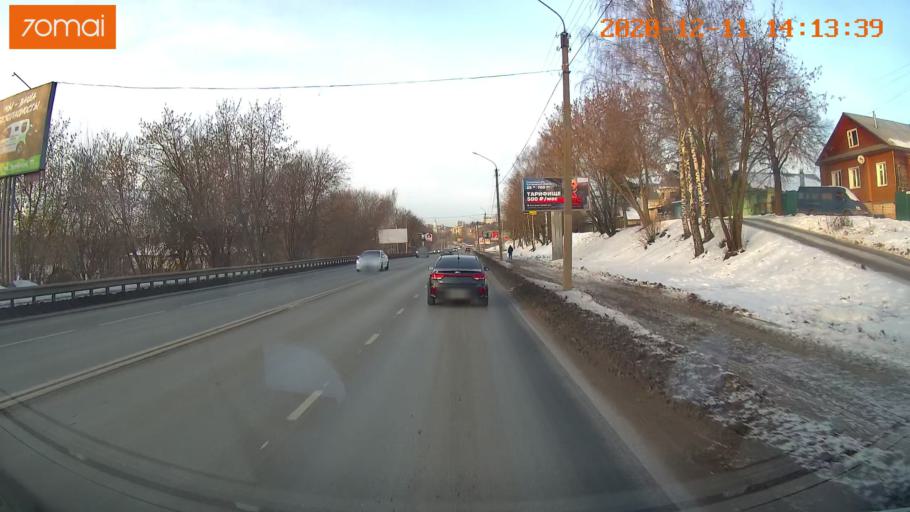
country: RU
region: Kostroma
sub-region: Kostromskoy Rayon
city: Kostroma
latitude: 57.7469
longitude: 40.9570
